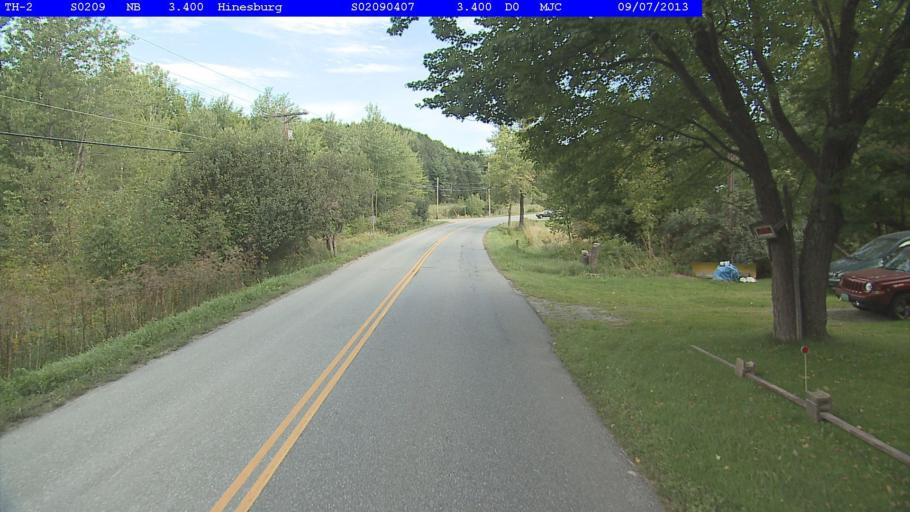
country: US
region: Vermont
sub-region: Chittenden County
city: Hinesburg
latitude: 44.3600
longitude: -73.0742
